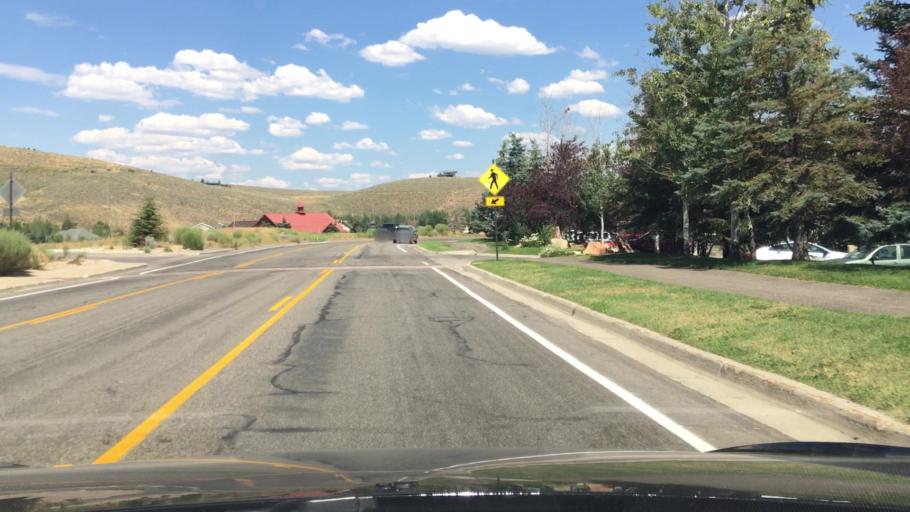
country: US
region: Utah
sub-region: Summit County
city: Snyderville
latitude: 40.7248
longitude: -111.5413
